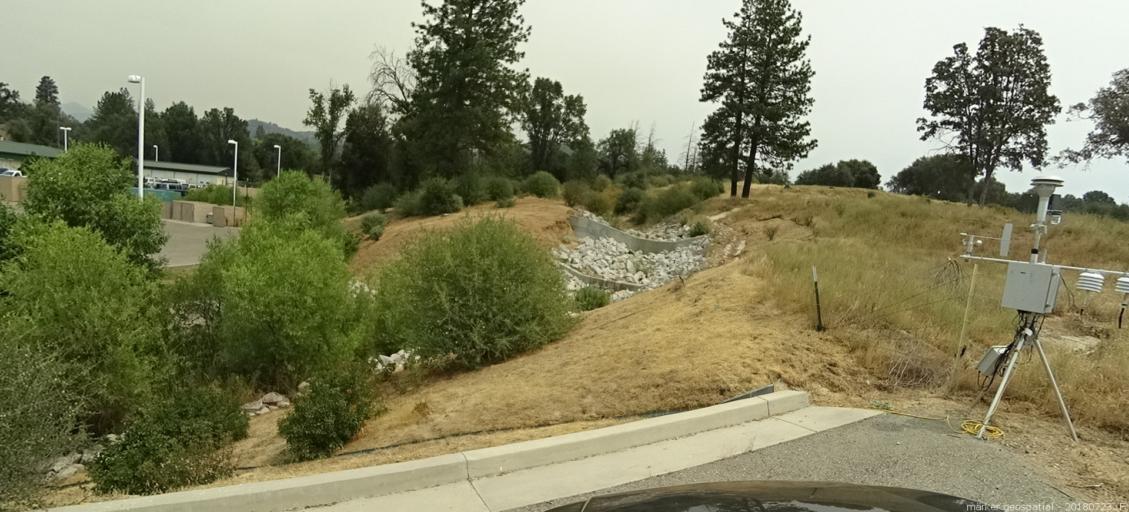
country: US
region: California
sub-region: Madera County
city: Oakhurst
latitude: 37.3397
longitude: -119.6666
